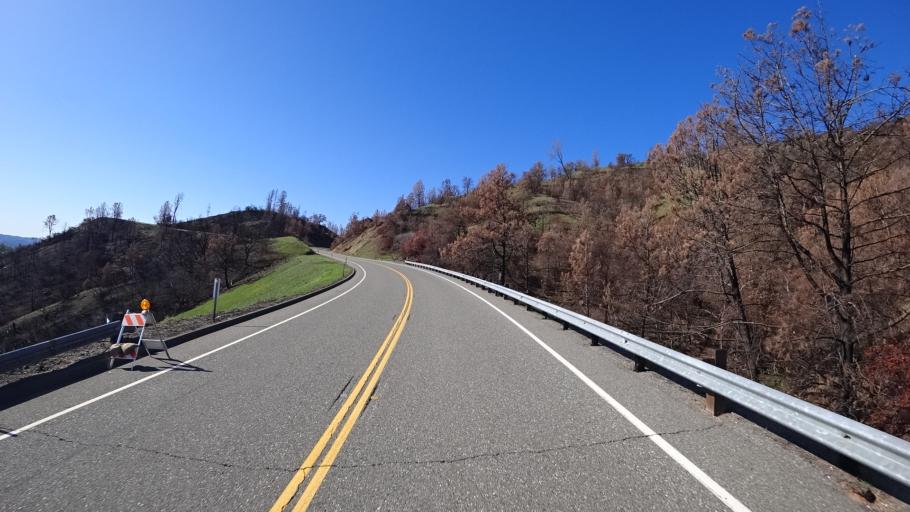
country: US
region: California
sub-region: Glenn County
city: Orland
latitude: 39.6481
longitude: -122.5973
